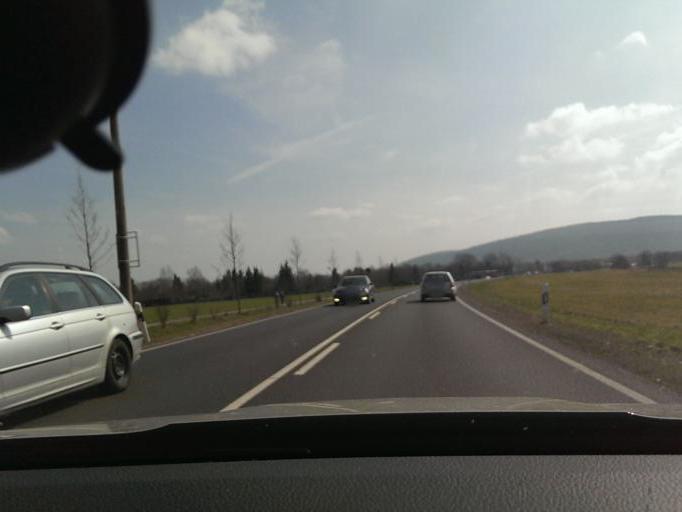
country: DE
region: Thuringia
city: Grafenhain
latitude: 50.8214
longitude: 10.7274
